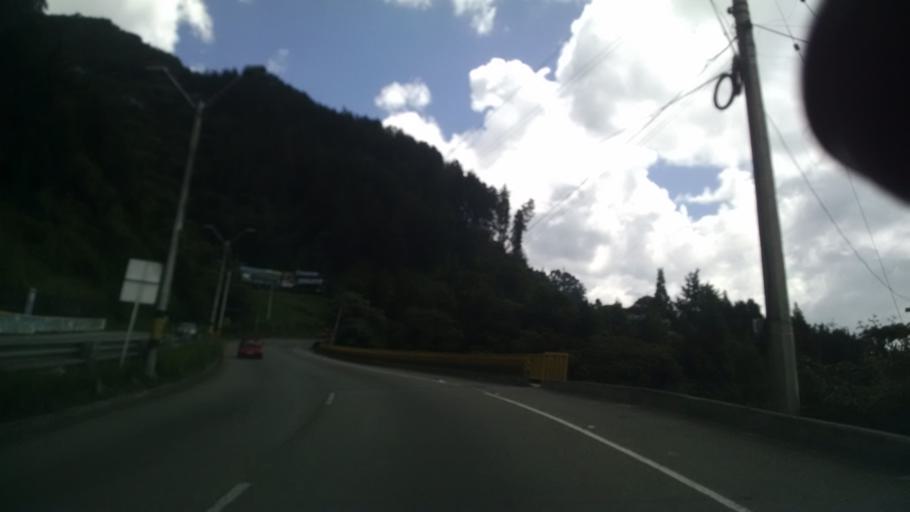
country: CO
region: Antioquia
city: Envigado
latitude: 6.1660
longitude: -75.5454
